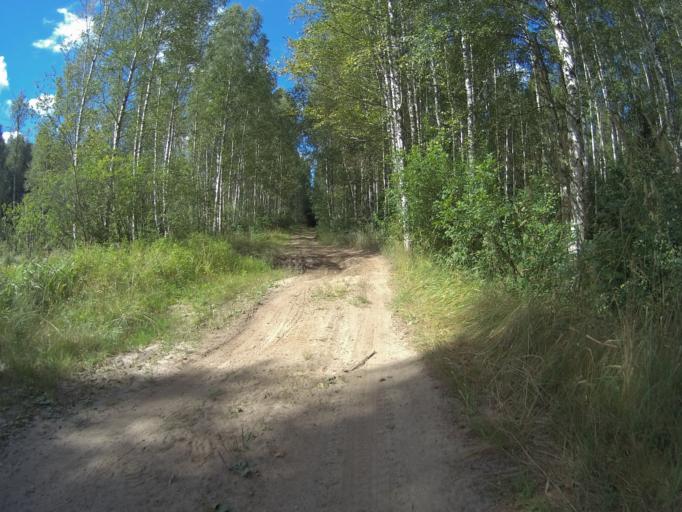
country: RU
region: Vladimir
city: Raduzhnyy
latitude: 55.9055
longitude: 40.2088
